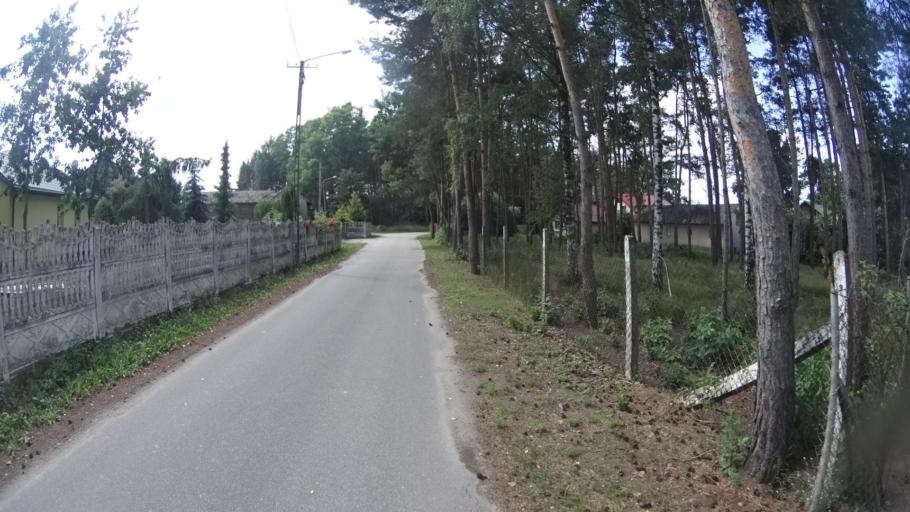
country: PL
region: Masovian Voivodeship
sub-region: Powiat bialobrzeski
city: Promna
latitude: 51.7114
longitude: 20.9089
